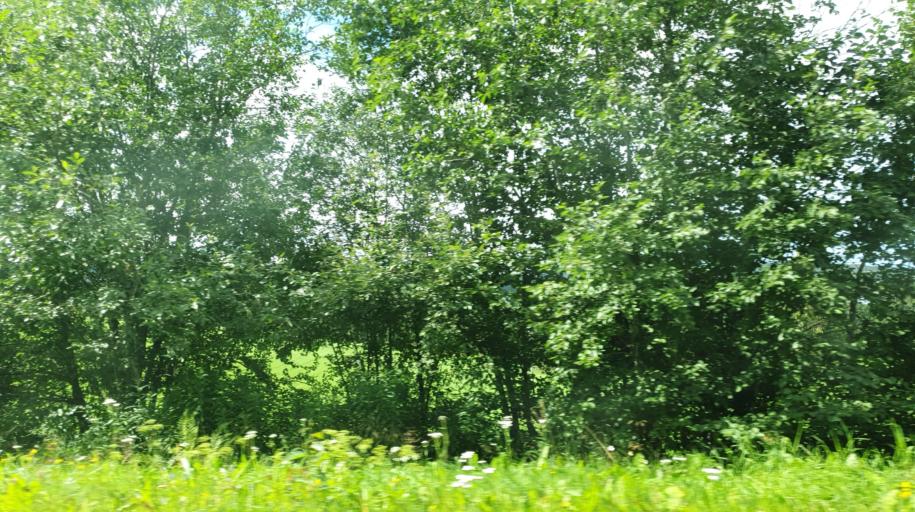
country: NO
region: Nord-Trondelag
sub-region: Levanger
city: Skogn
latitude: 63.6128
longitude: 11.2802
